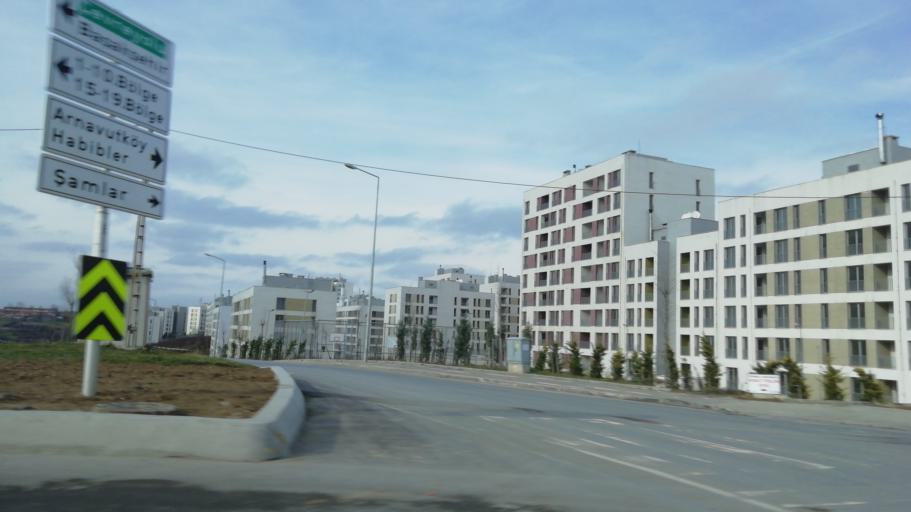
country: TR
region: Istanbul
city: Basaksehir
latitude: 41.1303
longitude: 28.7802
